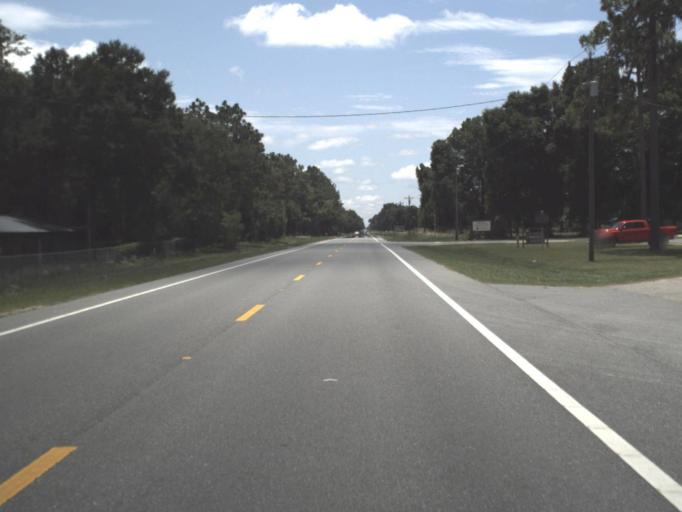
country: US
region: Florida
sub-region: Dixie County
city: Cross City
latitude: 29.7375
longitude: -82.9847
